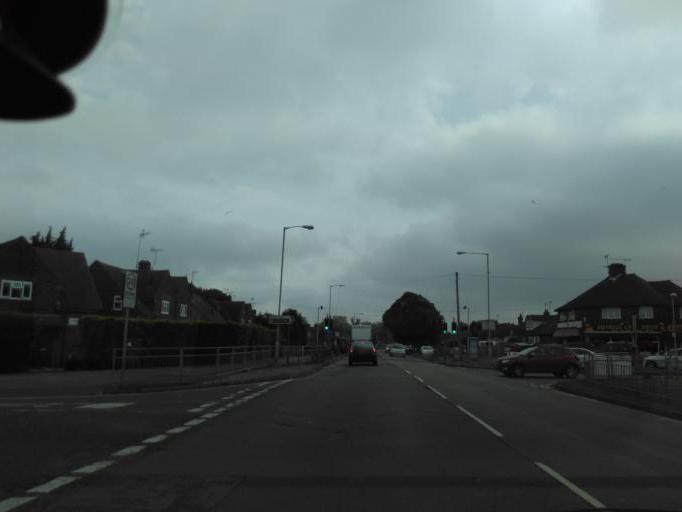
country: GB
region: England
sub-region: Kent
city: Sturry
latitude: 51.2913
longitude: 1.1021
